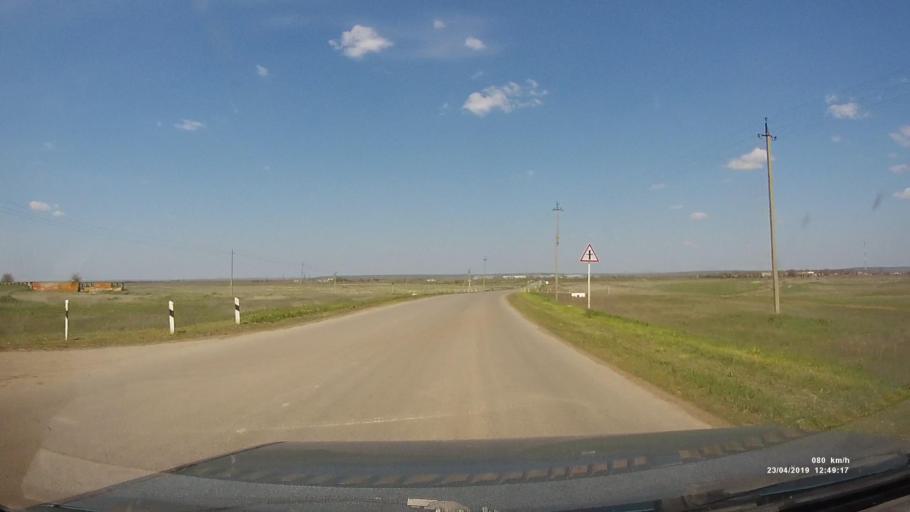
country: RU
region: Kalmykiya
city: Yashalta
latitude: 46.5354
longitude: 42.6389
